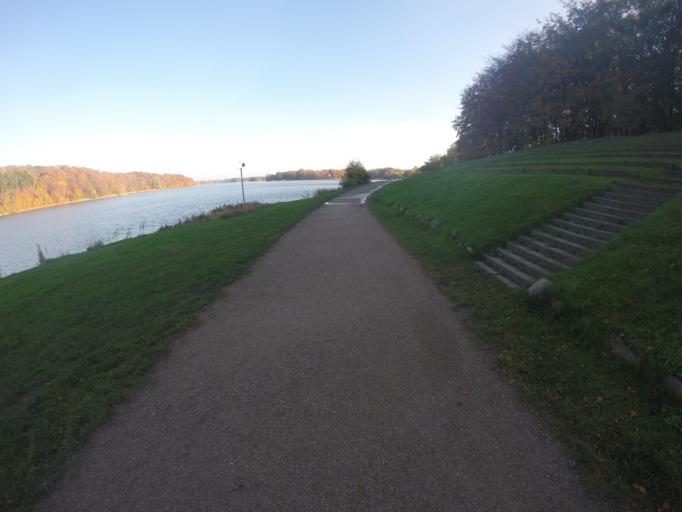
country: DK
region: Capital Region
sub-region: Rudersdal Kommune
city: Holte
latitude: 55.7748
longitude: 12.4402
